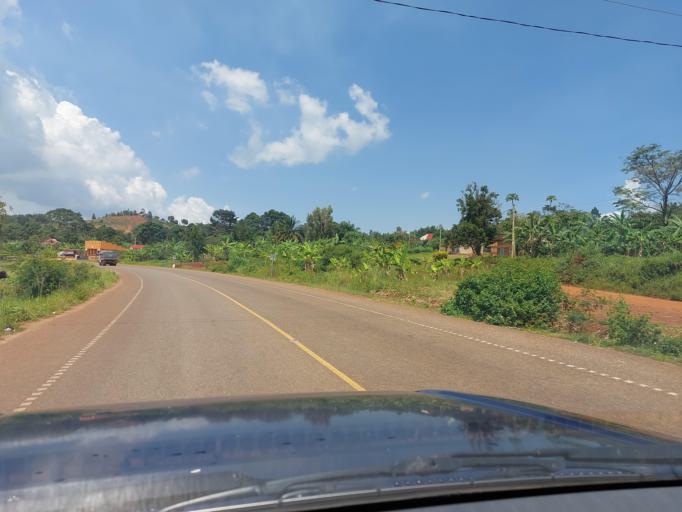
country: UG
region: Central Region
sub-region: Buikwe District
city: Buikwe
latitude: 0.2891
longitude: 33.0897
